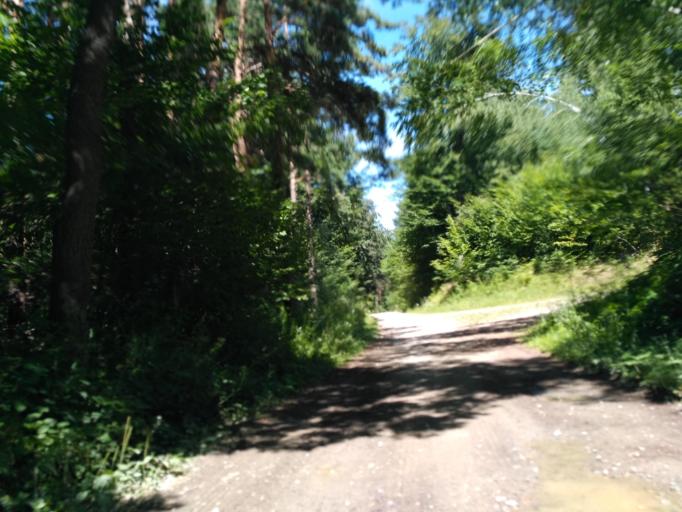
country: PL
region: Subcarpathian Voivodeship
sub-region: Powiat sanocki
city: Bukowsko
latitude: 49.4832
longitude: 22.0931
